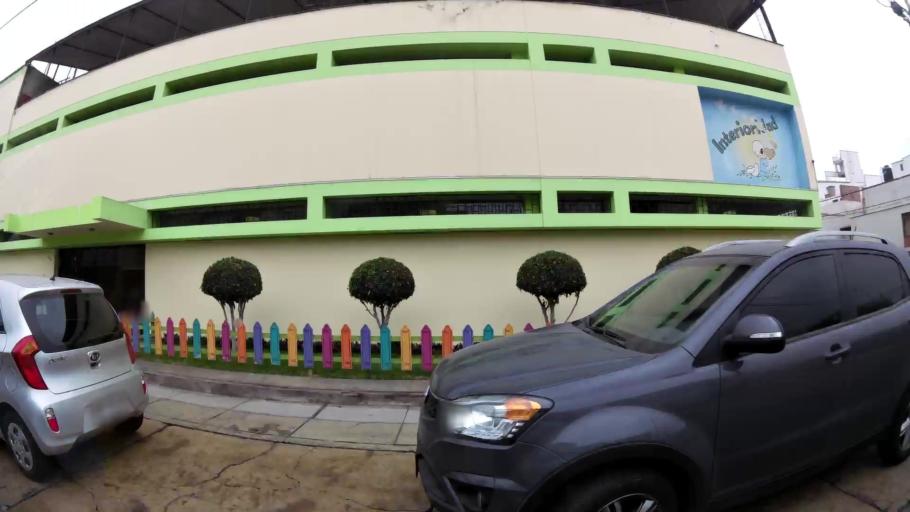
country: PE
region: Lima
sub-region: Lima
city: Surco
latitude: -12.1305
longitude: -77.0118
